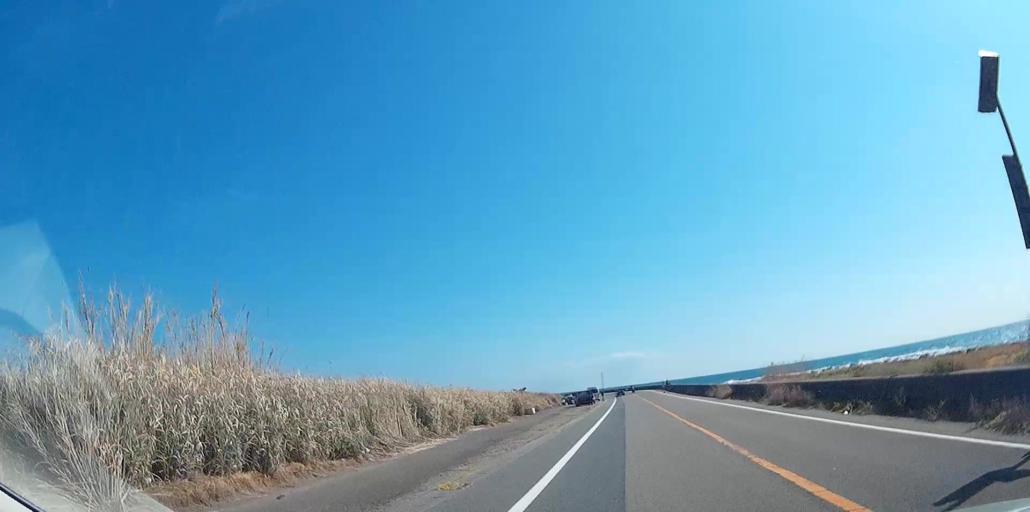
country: JP
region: Chiba
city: Tateyama
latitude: 34.9041
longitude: 139.8431
